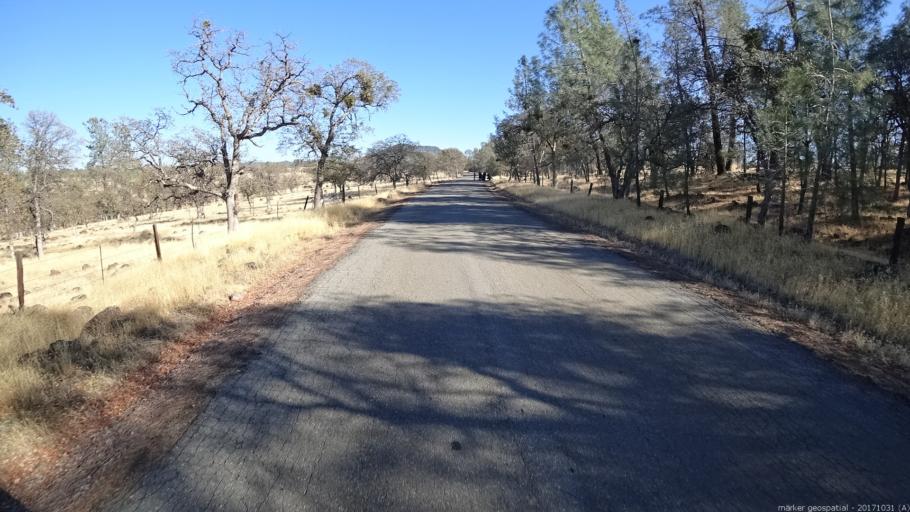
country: US
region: California
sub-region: Shasta County
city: Shingletown
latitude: 40.4582
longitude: -122.0396
